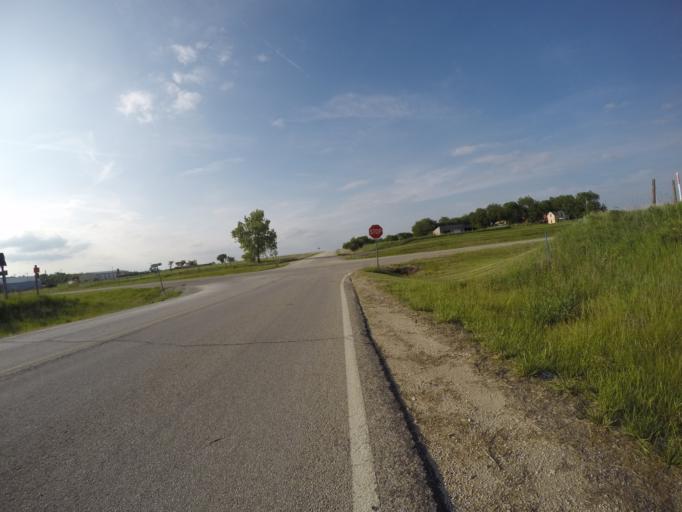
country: US
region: Kansas
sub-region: Pottawatomie County
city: Westmoreland
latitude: 39.4280
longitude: -96.6068
